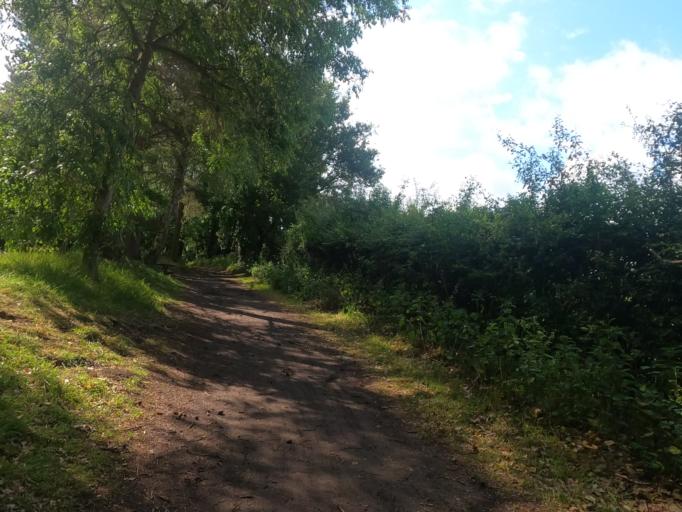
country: GB
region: England
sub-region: Cheshire West and Chester
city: Over
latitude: 53.2068
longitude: -2.5751
